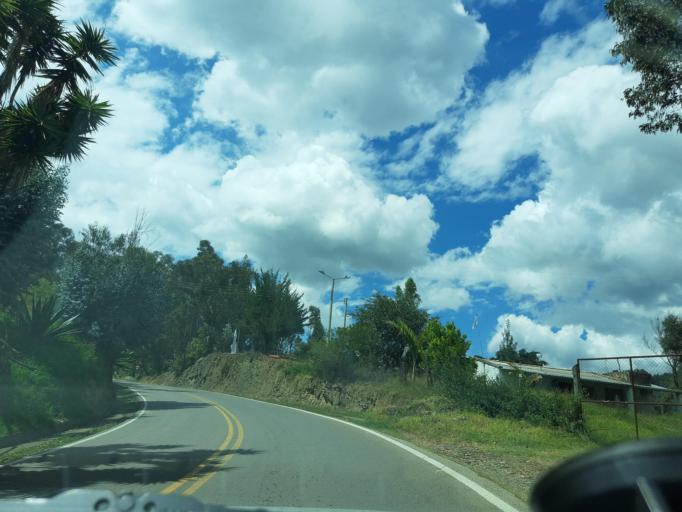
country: CO
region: Boyaca
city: Raquira
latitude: 5.5690
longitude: -73.6753
